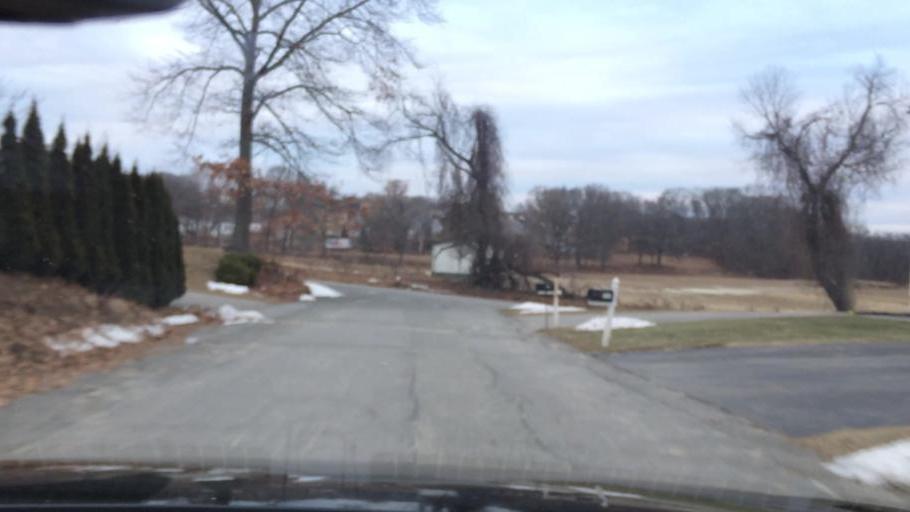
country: US
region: Massachusetts
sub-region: Essex County
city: North Andover
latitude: 42.7350
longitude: -71.1252
